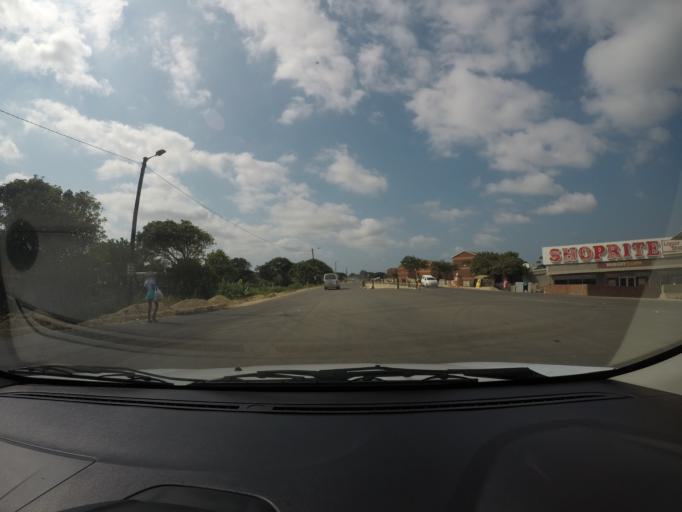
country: ZA
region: KwaZulu-Natal
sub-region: uThungulu District Municipality
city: eSikhawini
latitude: -28.8729
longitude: 31.9014
